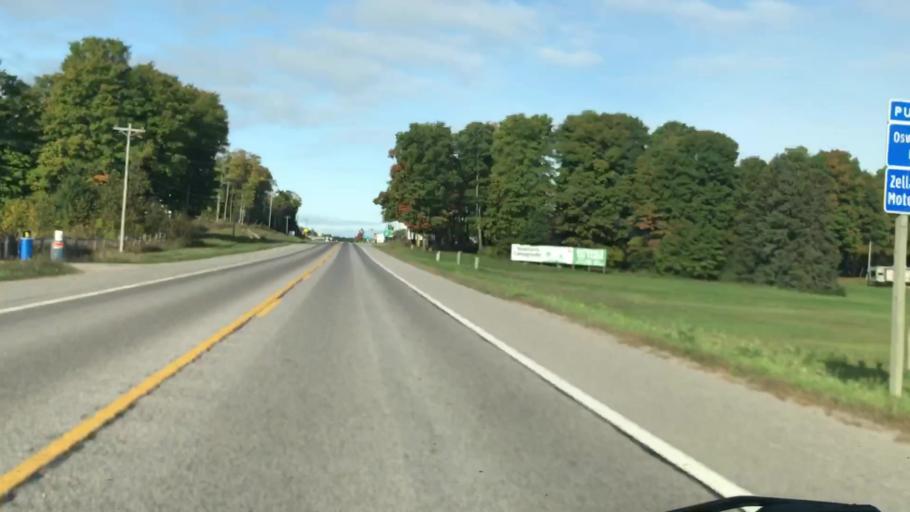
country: US
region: Michigan
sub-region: Luce County
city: Newberry
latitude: 46.3035
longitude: -85.5015
